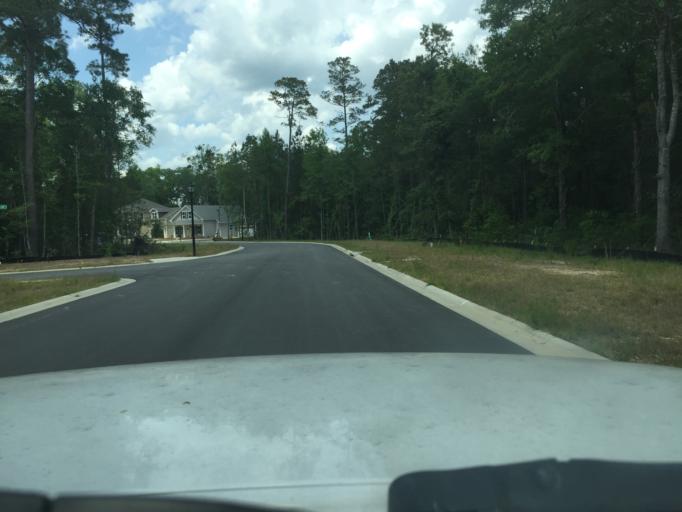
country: US
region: Georgia
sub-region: Chatham County
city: Georgetown
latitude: 32.0417
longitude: -81.2315
